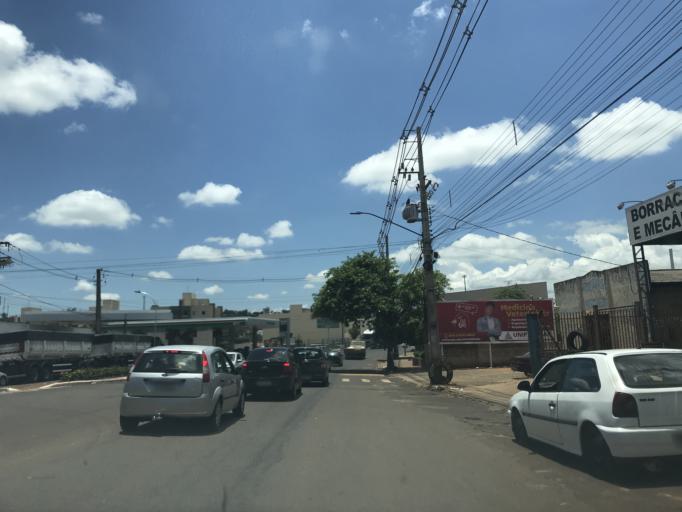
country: BR
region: Parana
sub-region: Marialva
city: Marialva
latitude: -23.4795
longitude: -51.8045
